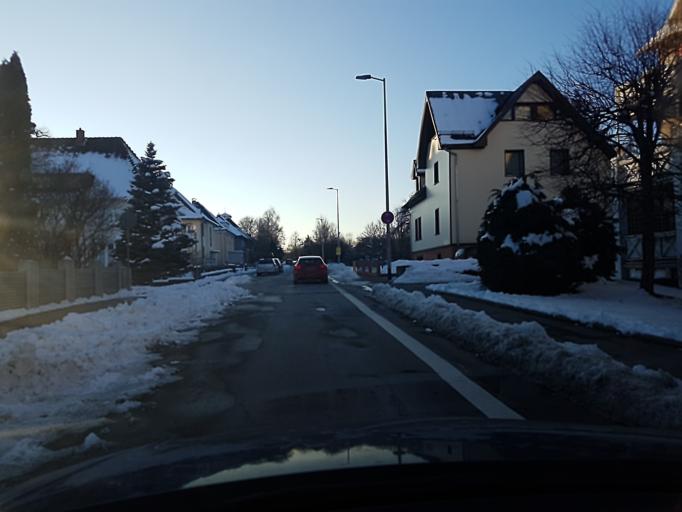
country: DE
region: Baden-Wuerttemberg
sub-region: Freiburg Region
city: Villingen-Schwenningen
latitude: 48.0568
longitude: 8.4527
